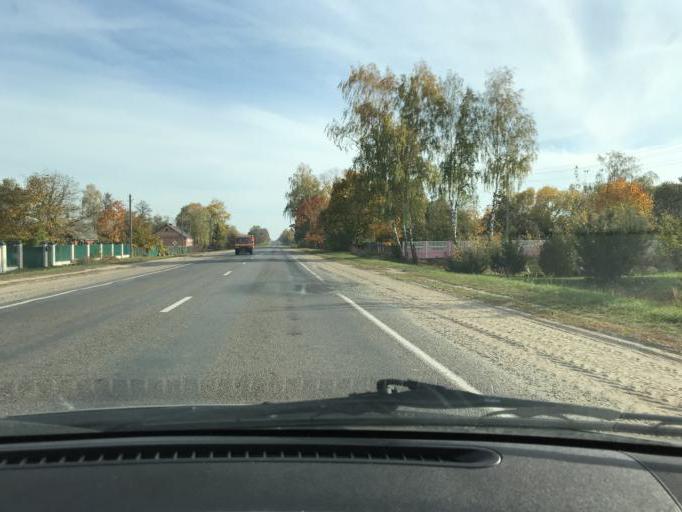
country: BY
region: Brest
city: Asnyezhytsy
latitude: 52.2209
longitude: 26.0324
